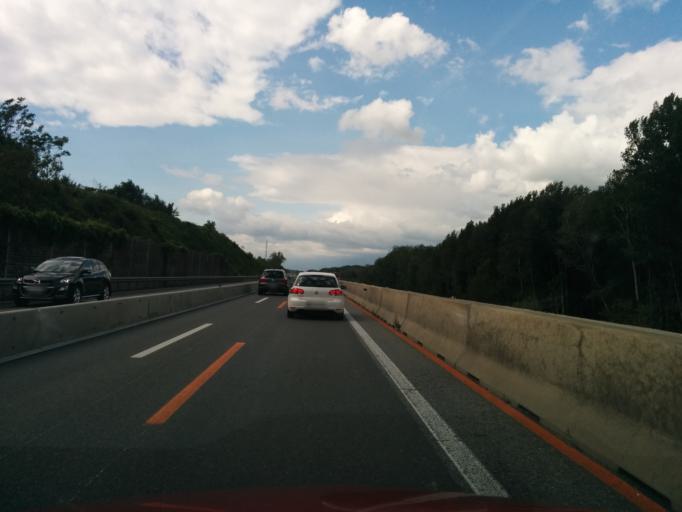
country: AT
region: Lower Austria
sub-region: Politischer Bezirk Wien-Umgebung
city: Fischamend Dorf
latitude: 48.1247
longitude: 16.6007
